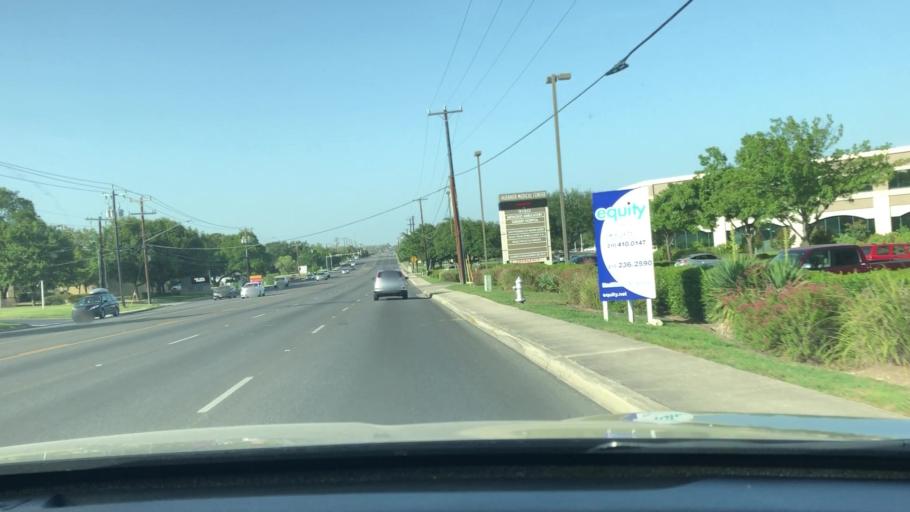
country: US
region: Texas
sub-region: Bexar County
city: Leon Valley
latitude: 29.5273
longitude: -98.5962
